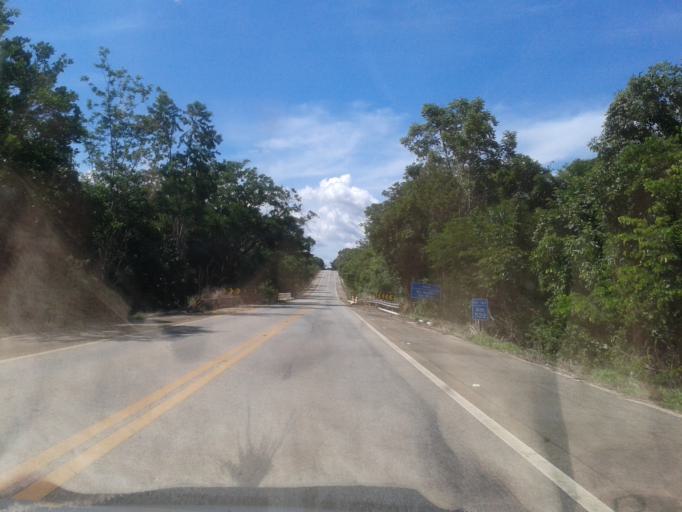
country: BR
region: Goias
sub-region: Goias
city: Goias
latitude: -15.7051
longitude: -50.1945
